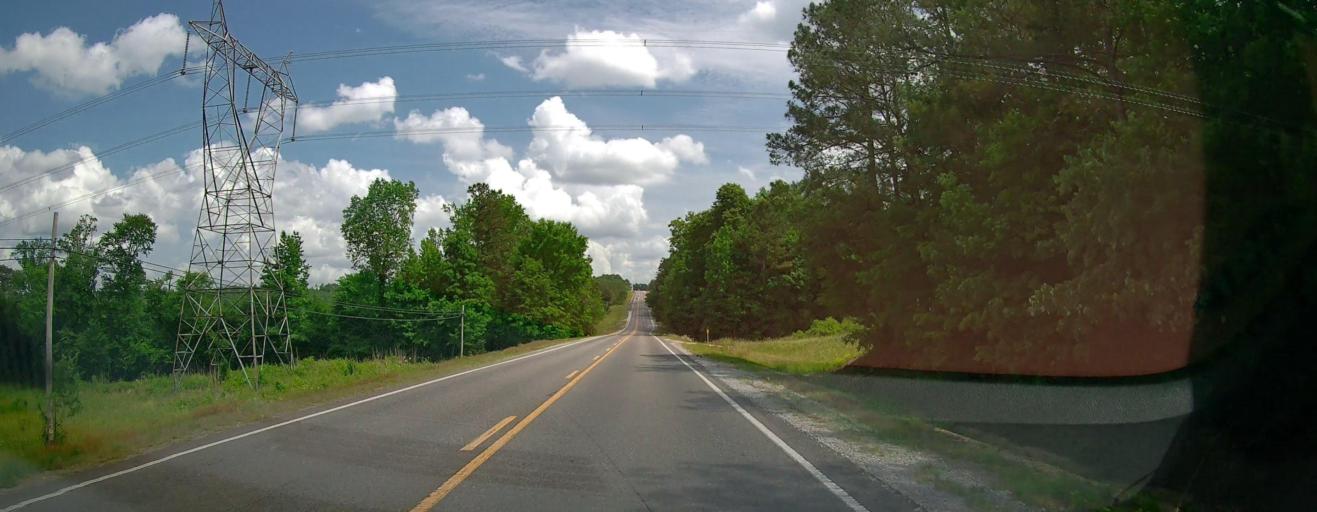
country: US
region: Alabama
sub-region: Marion County
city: Hamilton
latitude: 34.0924
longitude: -87.9845
